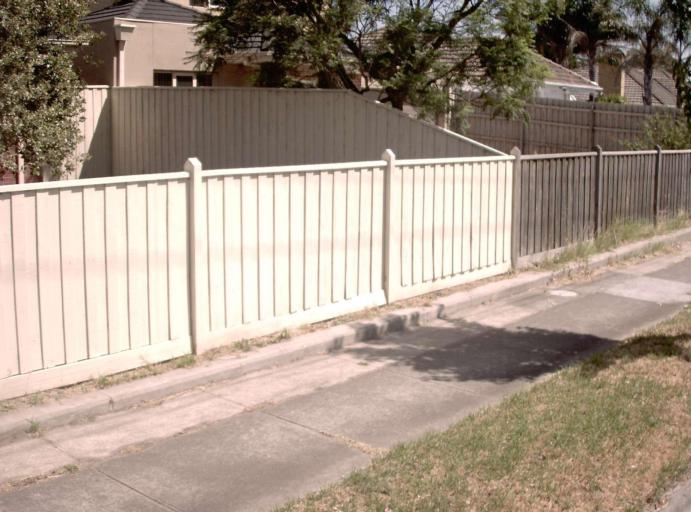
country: AU
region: Victoria
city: Ashburton
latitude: -37.8595
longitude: 145.0940
